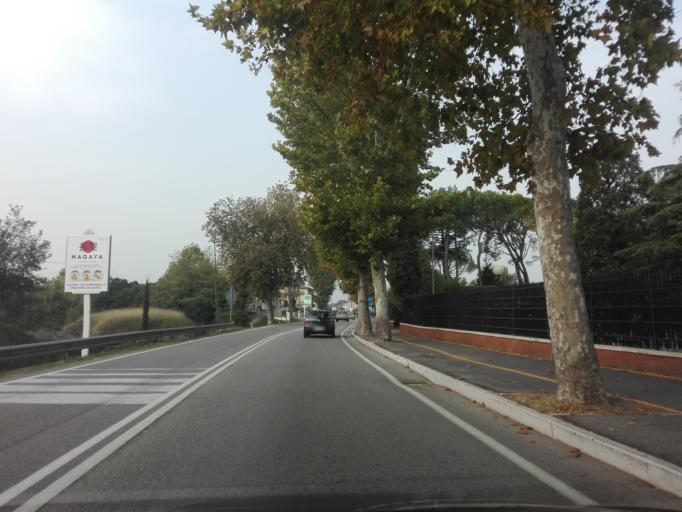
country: IT
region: Veneto
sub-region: Provincia di Verona
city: Peschiera del Garda
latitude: 45.4411
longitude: 10.6805
